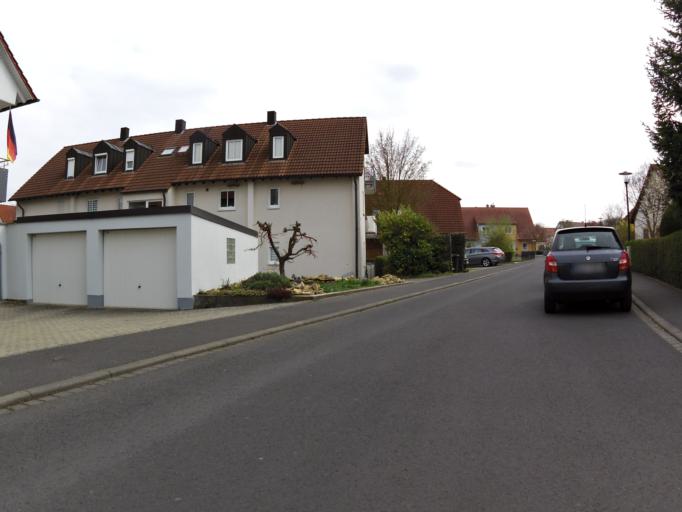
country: DE
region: Bavaria
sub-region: Regierungsbezirk Unterfranken
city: Rottendorf
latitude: 49.7927
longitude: 10.0212
